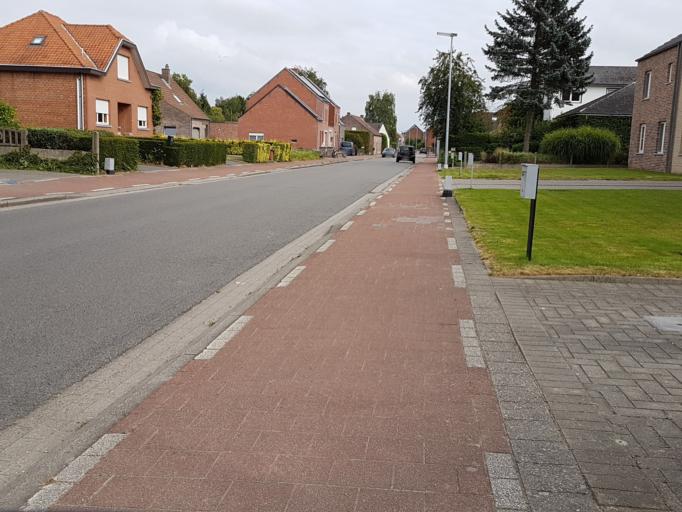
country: BE
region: Flanders
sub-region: Provincie Vlaams-Brabant
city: Haacht
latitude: 50.9610
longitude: 4.6216
